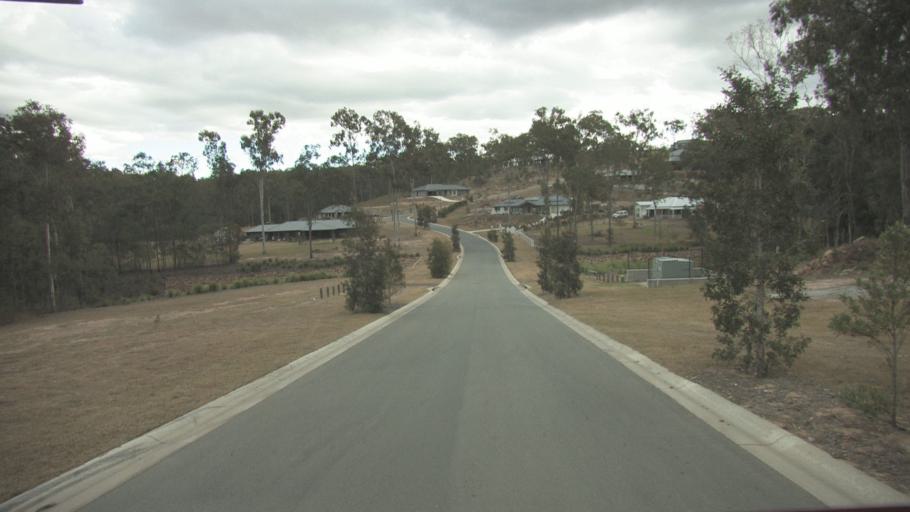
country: AU
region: Queensland
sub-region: Logan
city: Cedar Vale
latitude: -27.8597
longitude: 153.0799
